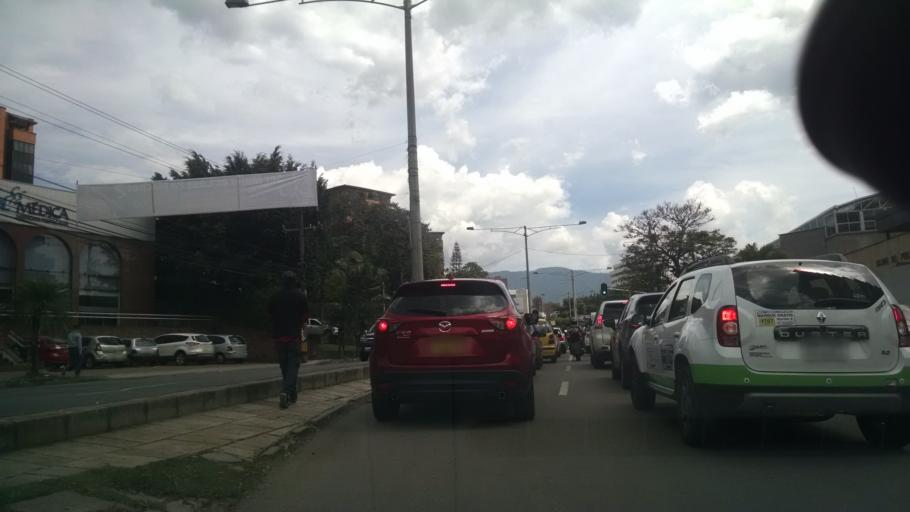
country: CO
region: Antioquia
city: Medellin
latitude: 6.2153
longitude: -75.5700
